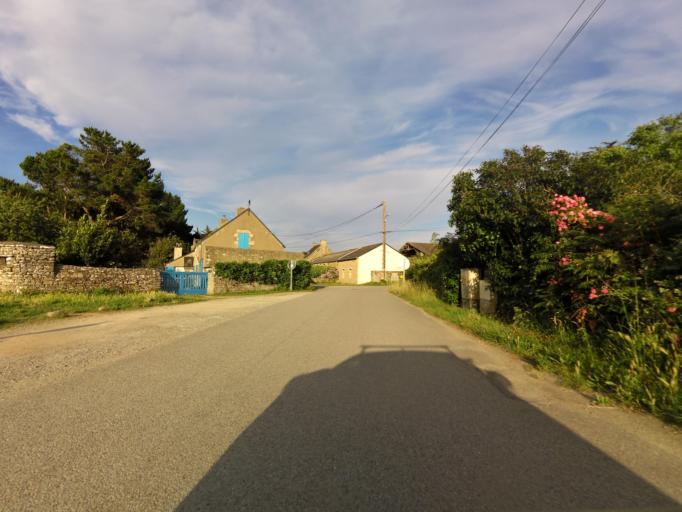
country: FR
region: Brittany
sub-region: Departement du Morbihan
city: Sene
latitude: 47.5880
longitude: -2.7157
